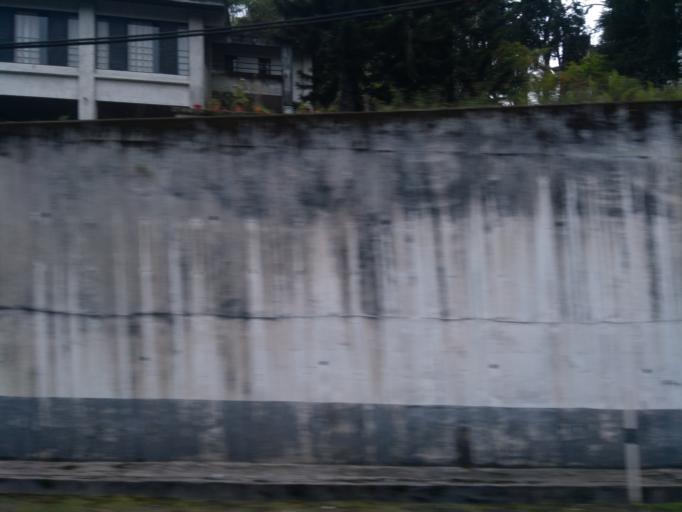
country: MY
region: Pahang
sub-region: Cameron Highlands
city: Tanah Rata
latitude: 4.4840
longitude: 101.3784
